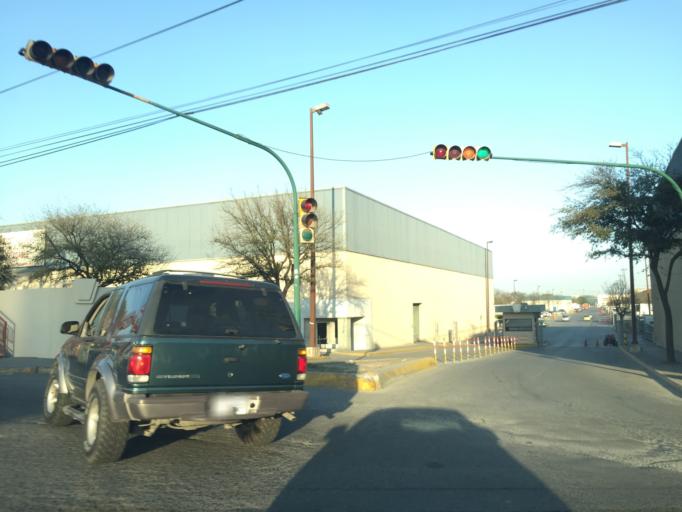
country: MX
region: Nuevo Leon
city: Guadalupe
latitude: 25.7041
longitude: -100.2246
